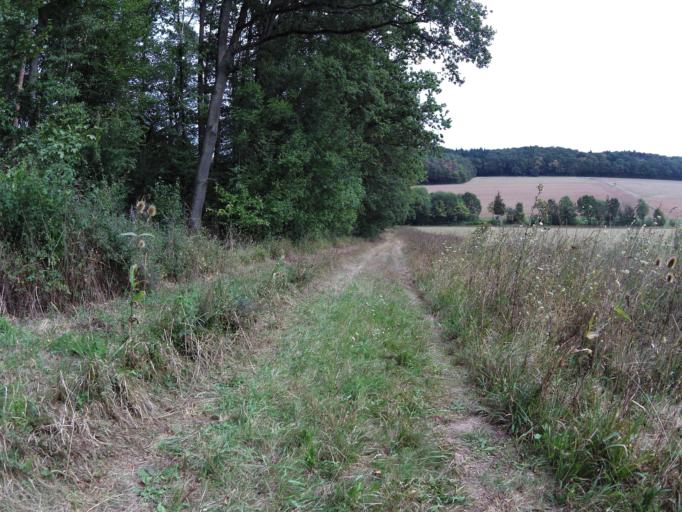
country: DE
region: Bavaria
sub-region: Regierungsbezirk Unterfranken
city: Kleinrinderfeld
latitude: 49.7119
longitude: 9.8281
